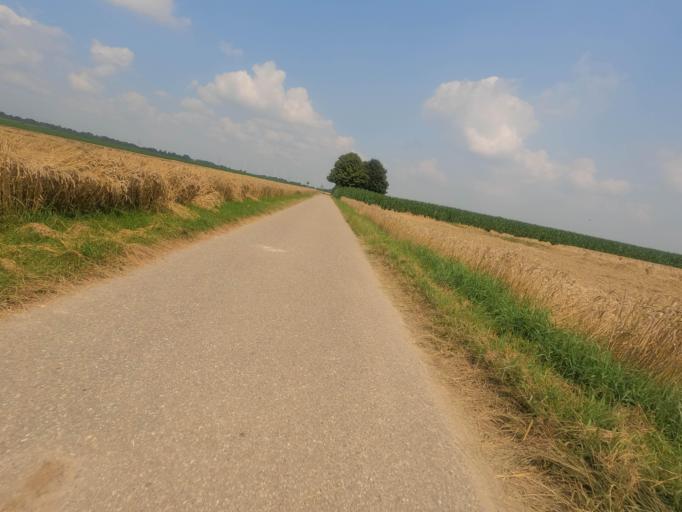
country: DE
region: North Rhine-Westphalia
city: Baesweiler
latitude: 50.9375
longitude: 6.1721
